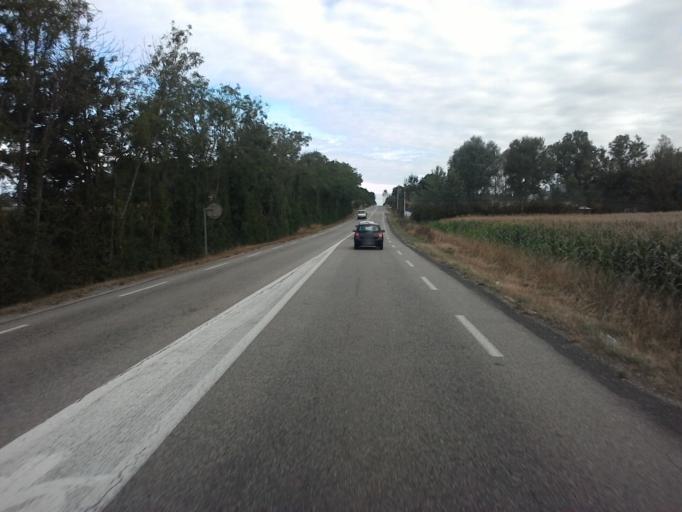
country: FR
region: Rhone-Alpes
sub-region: Departement de l'Ain
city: Saint-Martin-du-Mont
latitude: 46.0782
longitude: 5.3212
